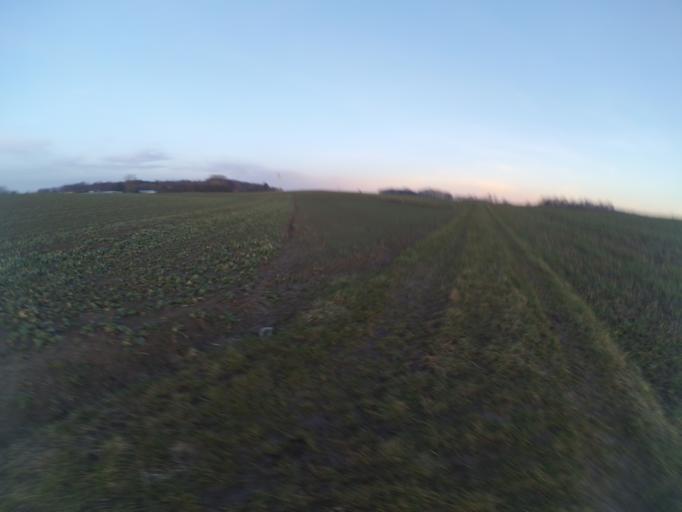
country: DE
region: Bavaria
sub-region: Swabia
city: Guenzburg
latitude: 48.4419
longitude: 10.2934
